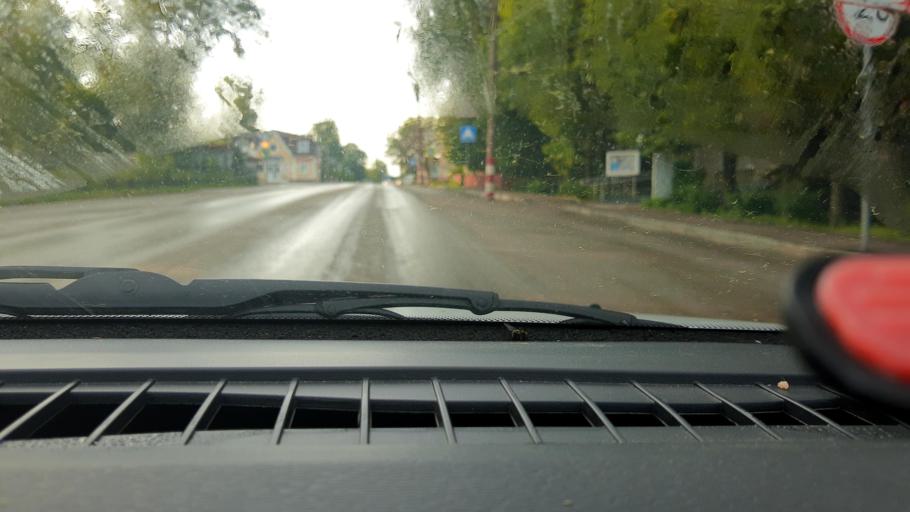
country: RU
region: Nizjnij Novgorod
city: Lukoyanov
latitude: 55.0348
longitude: 44.4947
